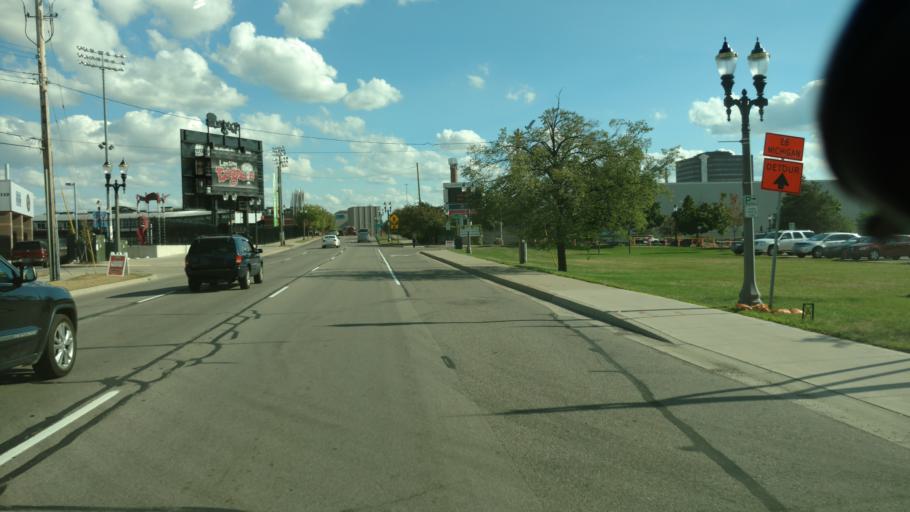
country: US
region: Michigan
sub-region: Ingham County
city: Lansing
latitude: 42.7364
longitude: -84.5466
